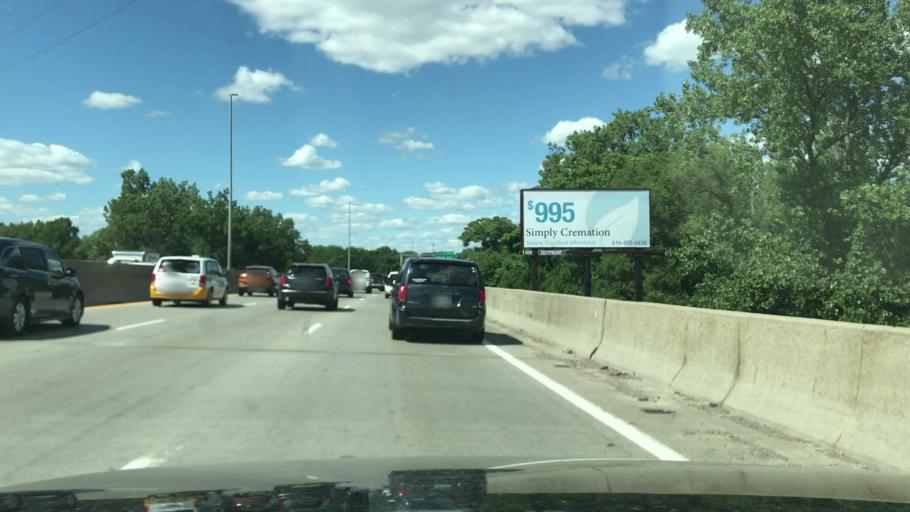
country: US
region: Michigan
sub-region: Kent County
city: Wyoming
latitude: 42.9241
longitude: -85.6820
